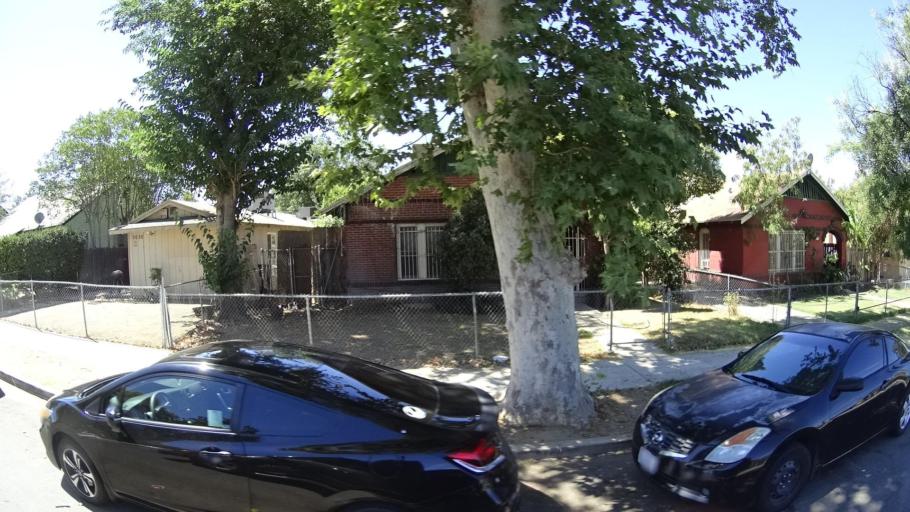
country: US
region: California
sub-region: Fresno County
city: Fresno
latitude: 36.7486
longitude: -119.7737
